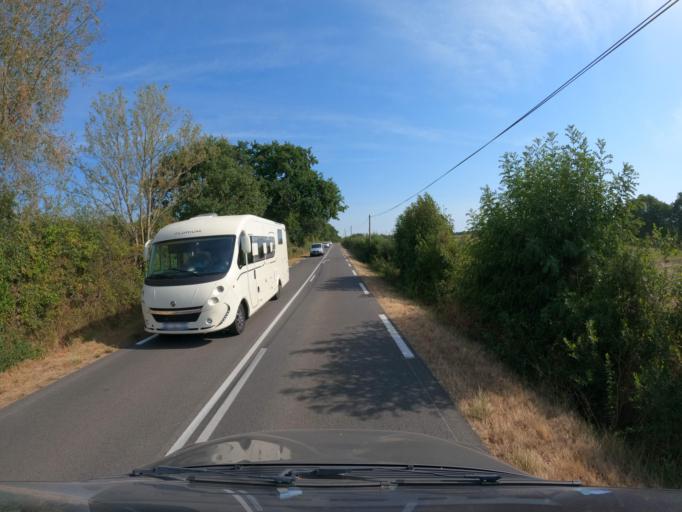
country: FR
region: Pays de la Loire
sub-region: Departement de la Vendee
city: Saint-Christophe-du-Ligneron
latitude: 46.8332
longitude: -1.7559
